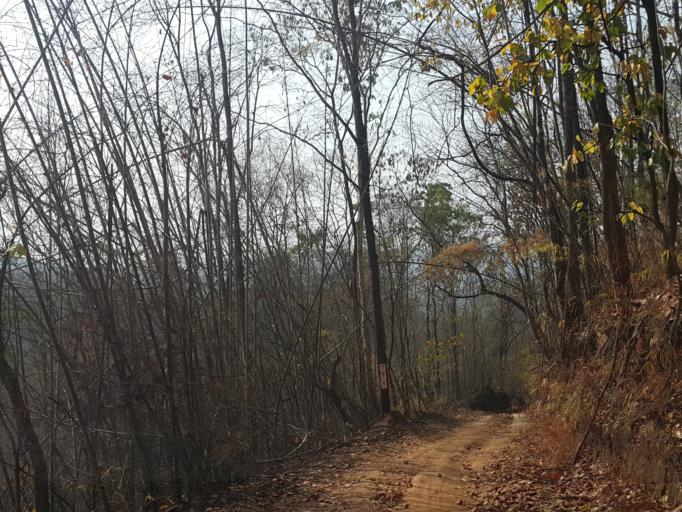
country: TH
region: Chiang Mai
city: Hang Dong
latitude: 18.7493
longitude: 98.8581
